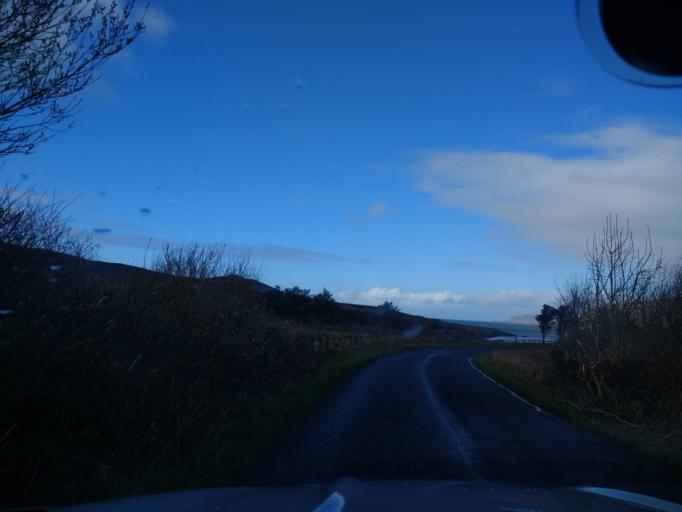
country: IE
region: Ulster
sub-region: County Donegal
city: Buncrana
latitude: 55.1666
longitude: -7.5743
